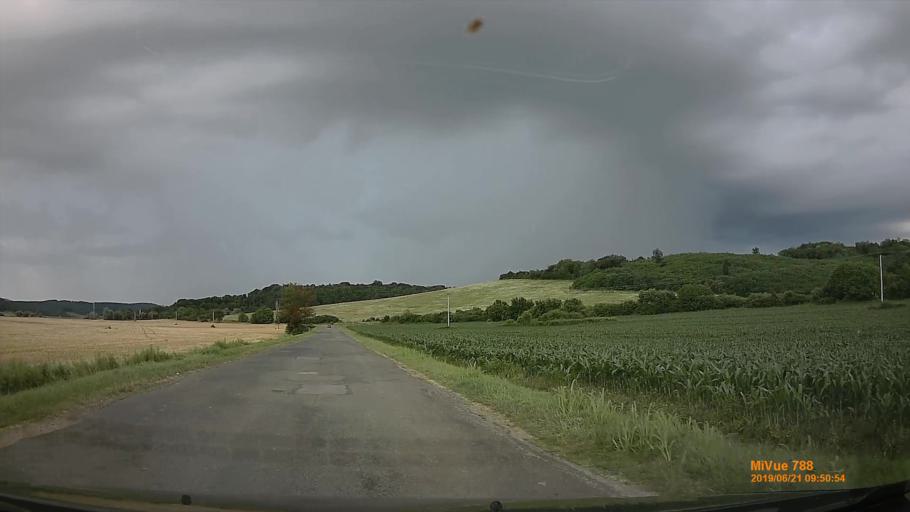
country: HU
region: Baranya
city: Sasd
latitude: 46.2566
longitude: 18.0270
